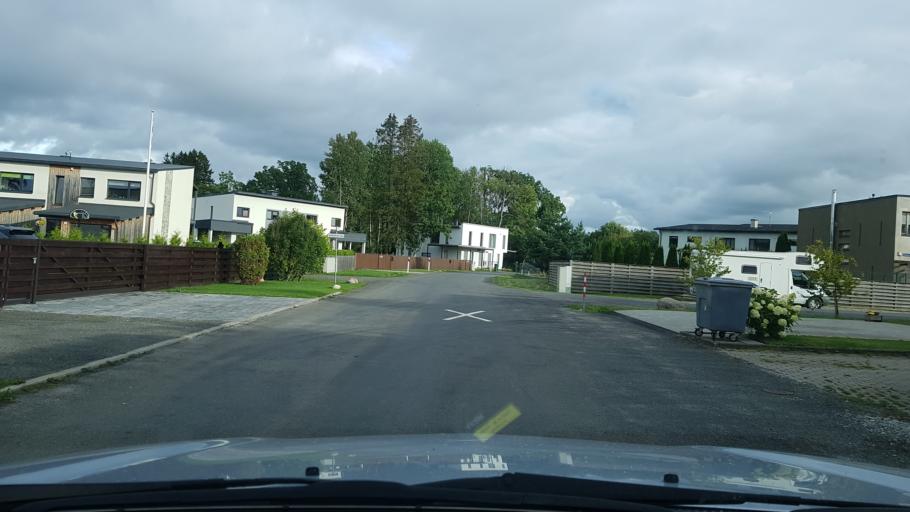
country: EE
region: Harju
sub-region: Rae vald
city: Jueri
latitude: 59.3644
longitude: 24.9201
